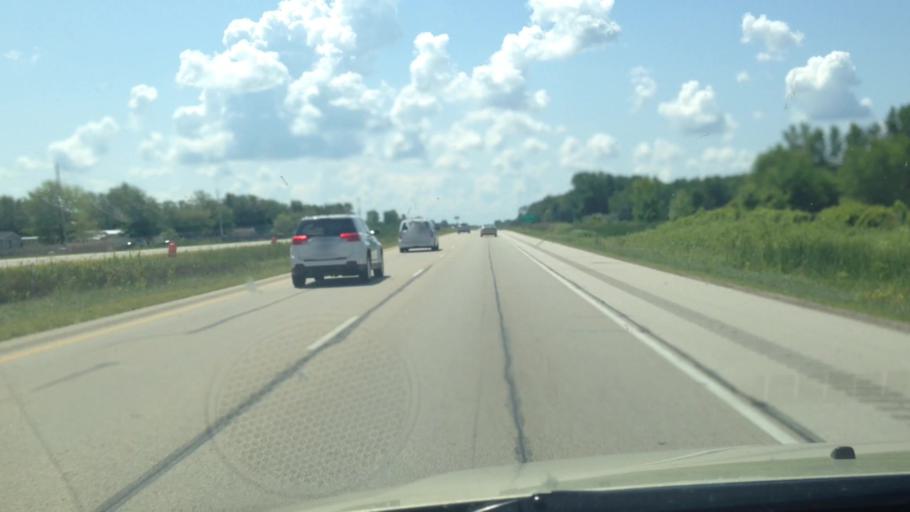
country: US
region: Wisconsin
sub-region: Brown County
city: Suamico
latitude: 44.6993
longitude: -88.0509
